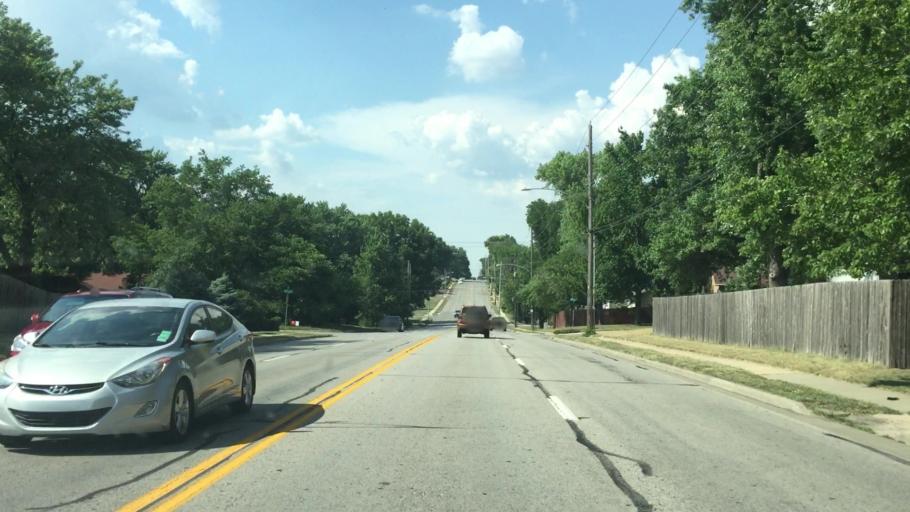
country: US
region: Kansas
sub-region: Johnson County
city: Merriam
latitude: 38.9969
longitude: -94.7145
